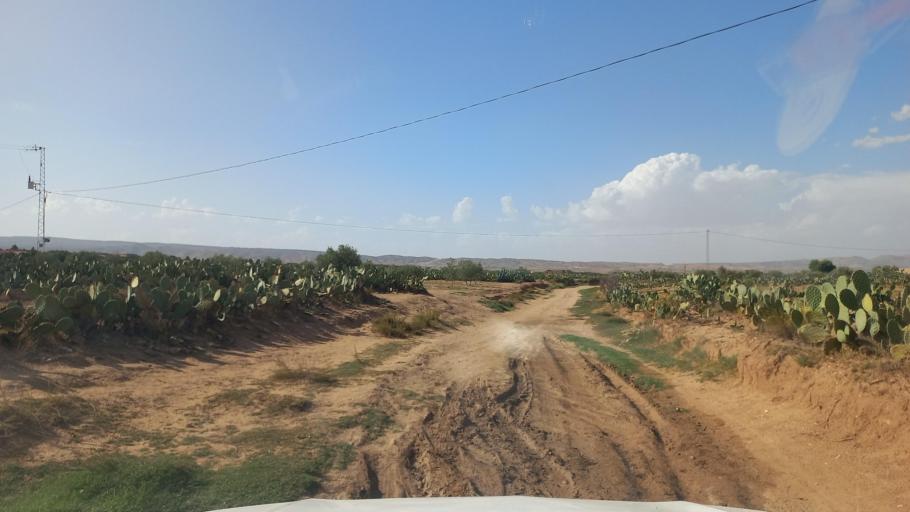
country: TN
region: Al Qasrayn
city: Sbiba
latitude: 35.3121
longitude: 9.0320
